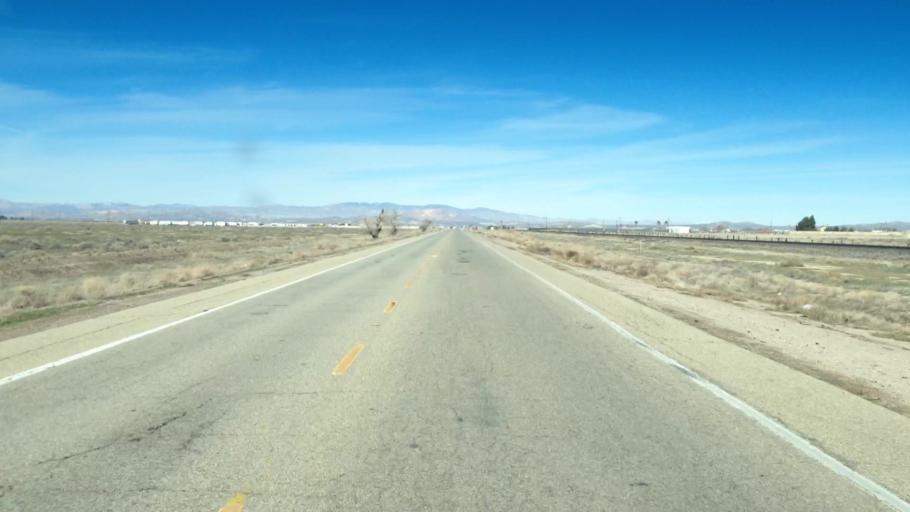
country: US
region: California
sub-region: Los Angeles County
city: Lancaster
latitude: 34.7267
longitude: -118.1411
